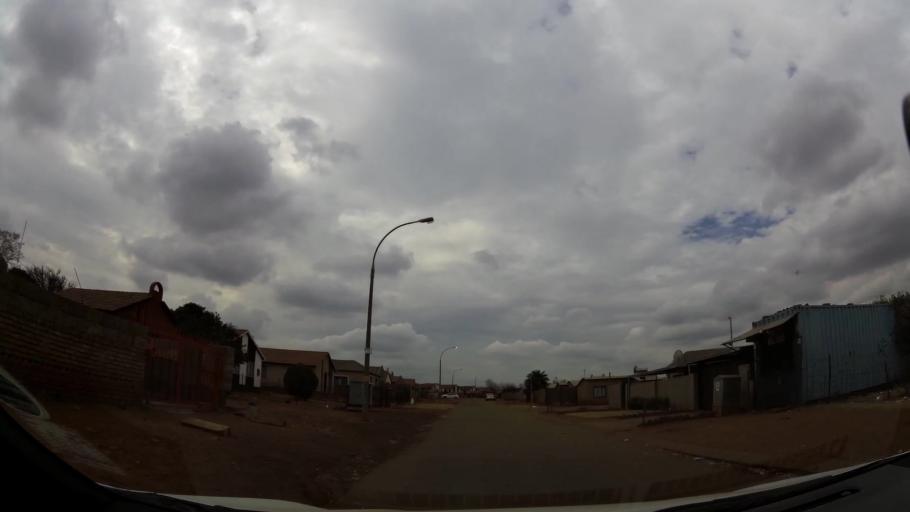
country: ZA
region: Gauteng
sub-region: Ekurhuleni Metropolitan Municipality
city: Germiston
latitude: -26.3834
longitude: 28.1234
